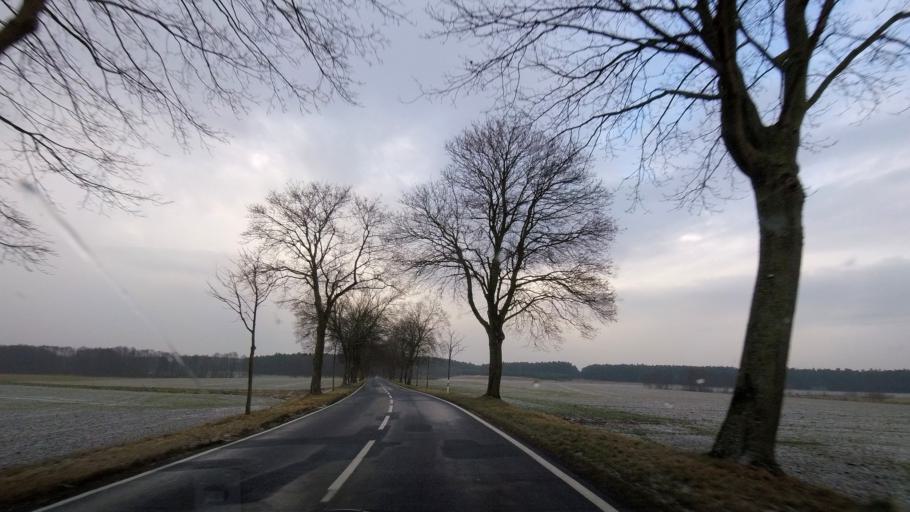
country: DE
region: Brandenburg
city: Treuenbrietzen
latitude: 52.0562
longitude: 12.9430
